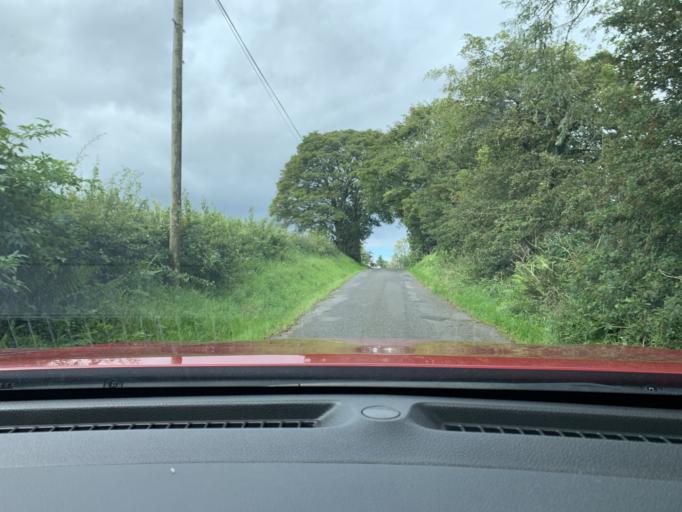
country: IE
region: Connaught
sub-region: Sligo
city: Collooney
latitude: 54.1542
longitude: -8.4269
